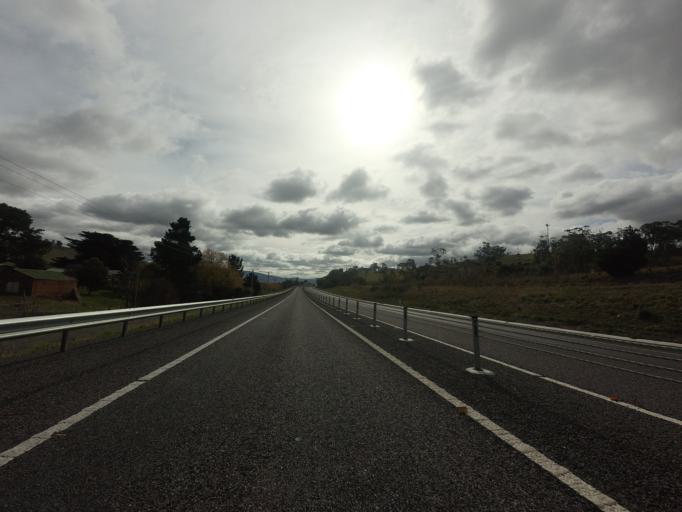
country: AU
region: Tasmania
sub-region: Brighton
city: Bridgewater
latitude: -42.5500
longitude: 147.2089
